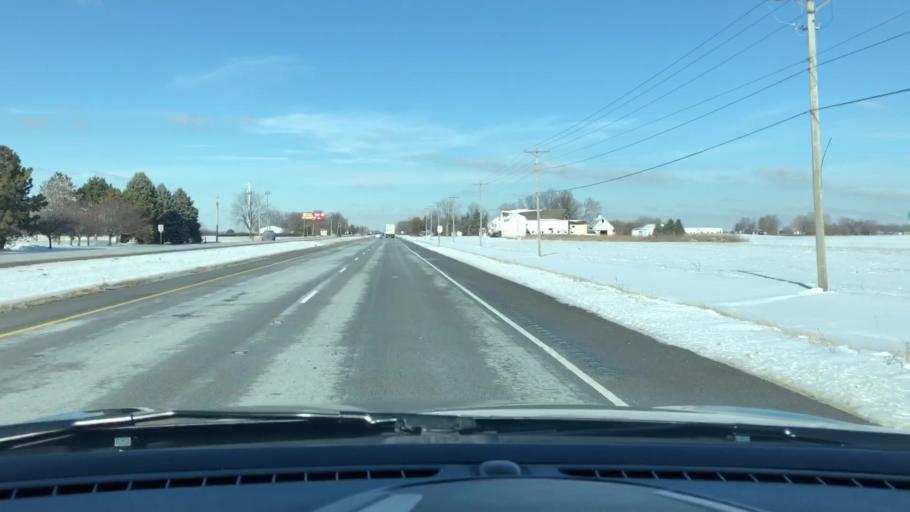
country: US
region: Illinois
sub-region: Will County
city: Preston Heights
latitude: 41.4688
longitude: -88.0796
